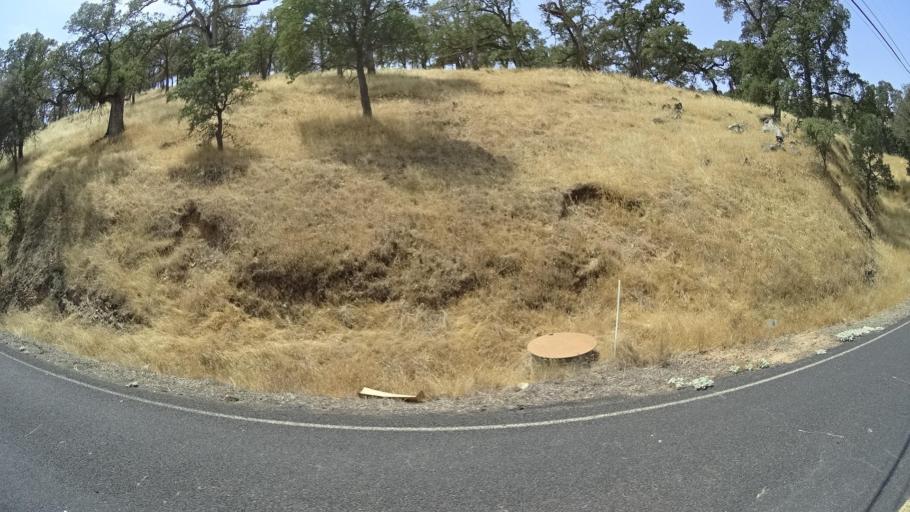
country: US
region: California
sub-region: Tuolumne County
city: Jamestown
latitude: 37.6619
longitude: -120.3494
